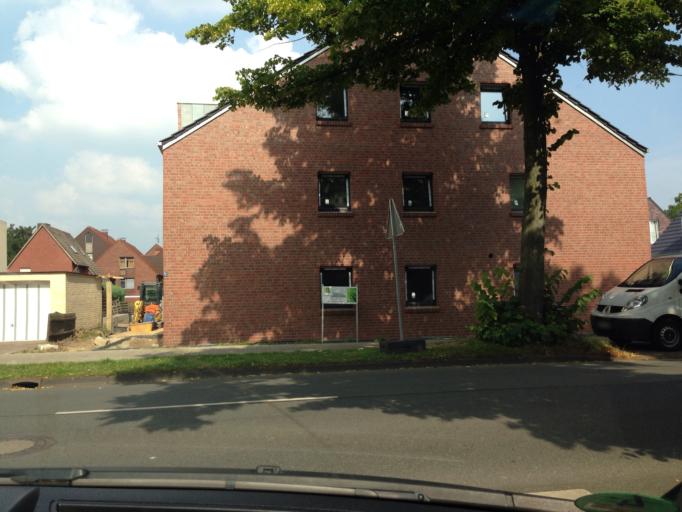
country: DE
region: North Rhine-Westphalia
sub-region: Regierungsbezirk Munster
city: Muenster
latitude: 51.9571
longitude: 7.5314
